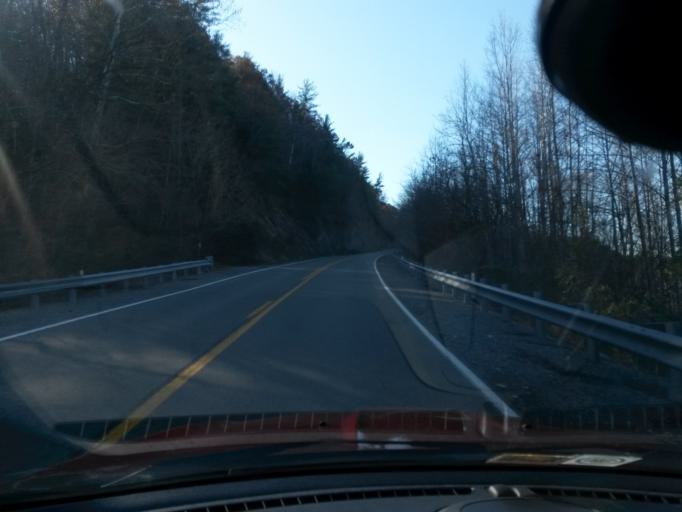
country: US
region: Virginia
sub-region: Botetourt County
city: Buchanan
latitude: 37.5842
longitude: -79.7287
